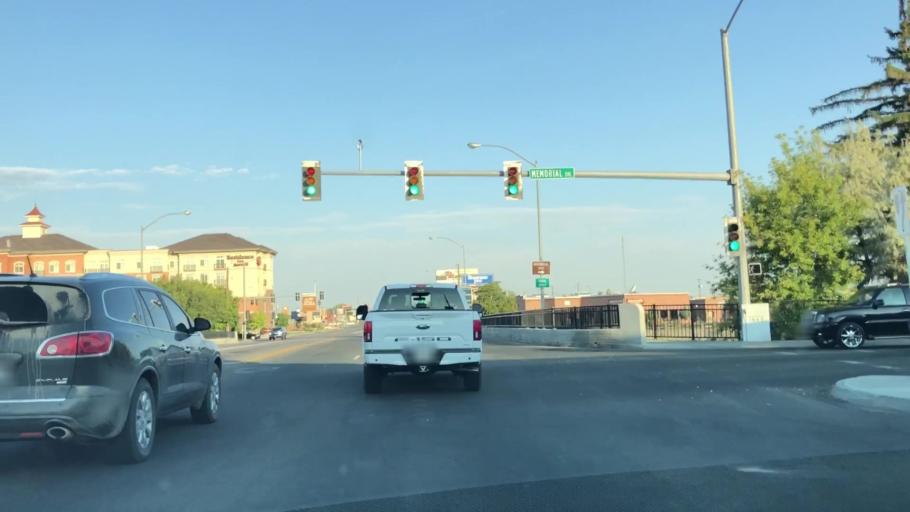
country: US
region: Idaho
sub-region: Bonneville County
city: Idaho Falls
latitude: 43.4927
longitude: -112.0437
